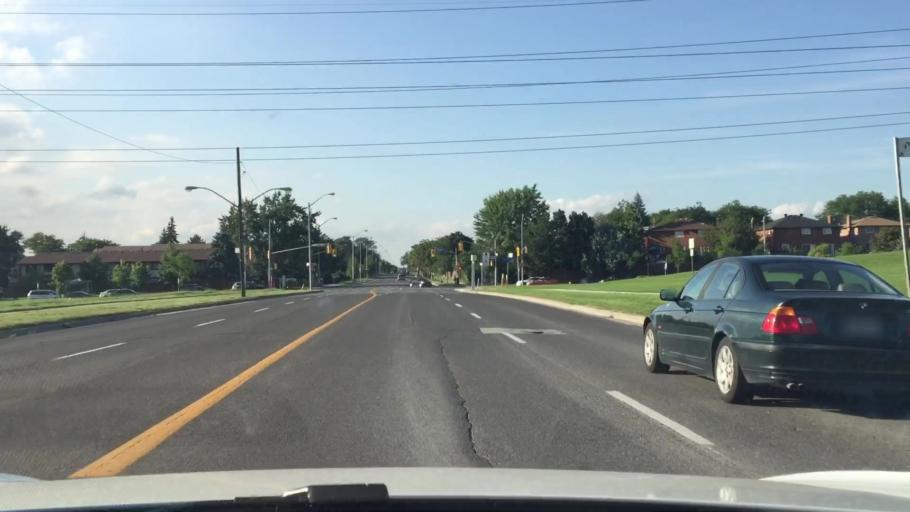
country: CA
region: Ontario
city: Scarborough
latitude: 43.8076
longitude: -79.3107
